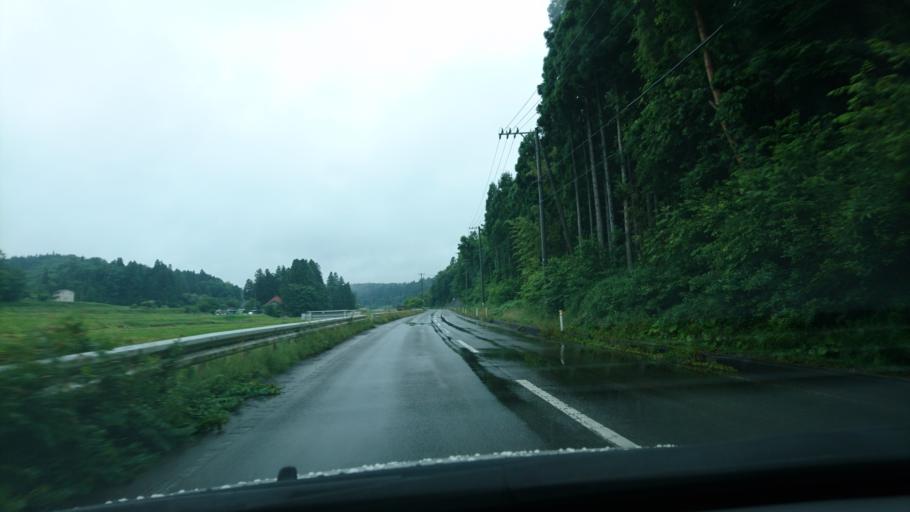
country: JP
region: Iwate
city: Ichinoseki
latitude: 38.9364
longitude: 141.0469
